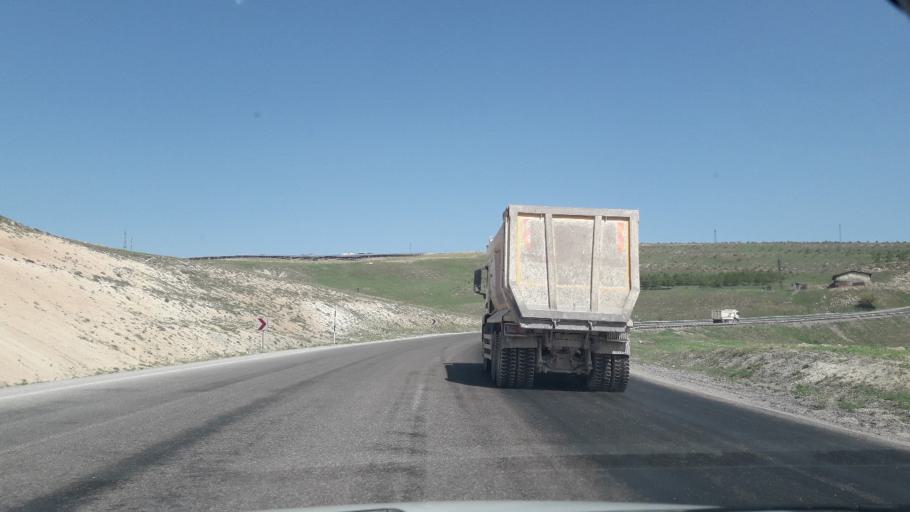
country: TR
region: Sivas
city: Deliktas
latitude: 39.3178
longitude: 37.1395
